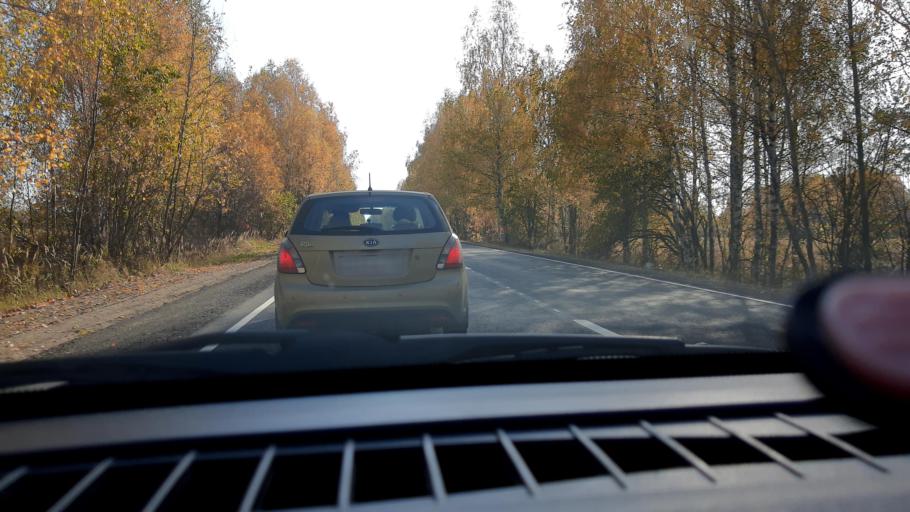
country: RU
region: Nizjnij Novgorod
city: Novaya Balakhna
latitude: 56.5557
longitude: 43.7395
